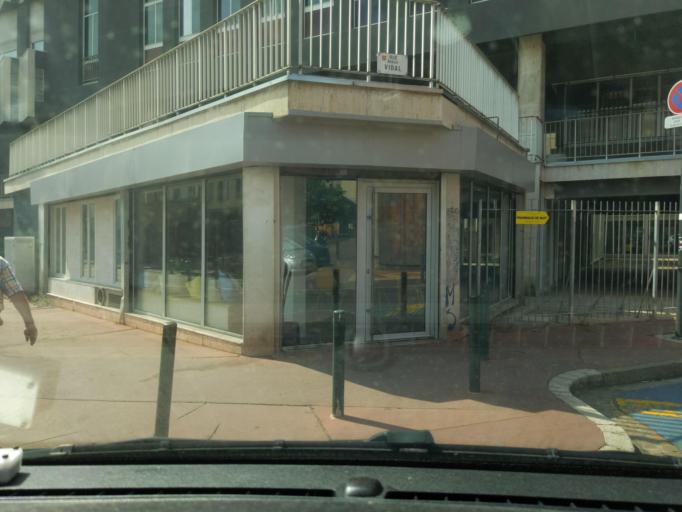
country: FR
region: Midi-Pyrenees
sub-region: Departement de la Haute-Garonne
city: Toulouse
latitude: 43.6071
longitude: 1.4529
